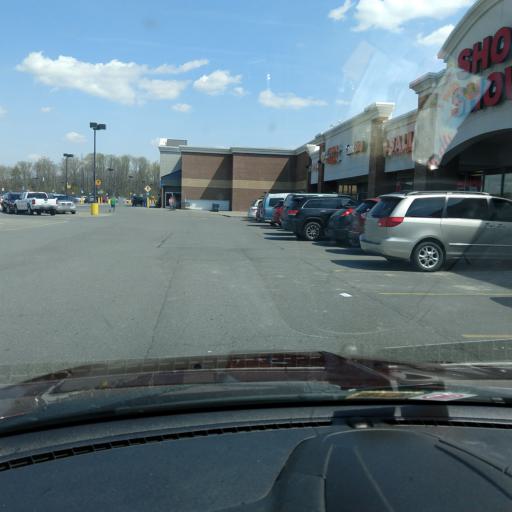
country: US
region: West Virginia
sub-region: Fayette County
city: Fayetteville
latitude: 38.0332
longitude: -81.1203
